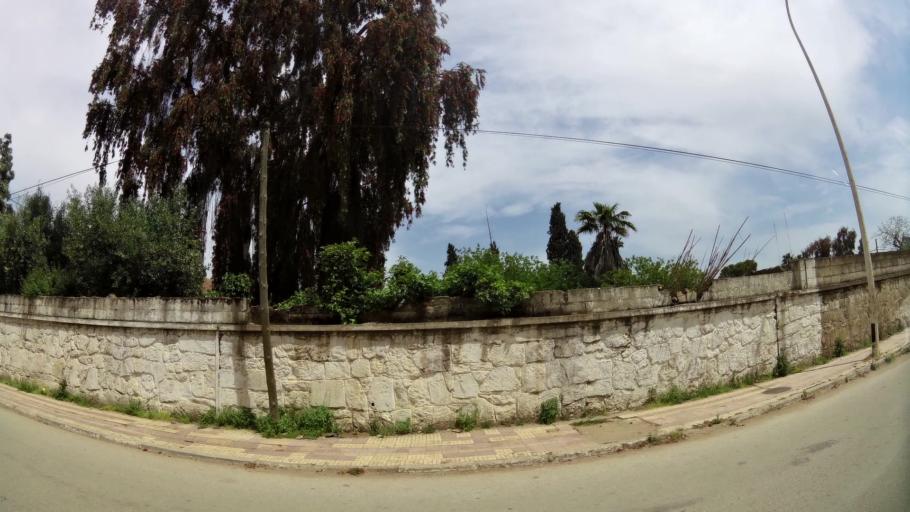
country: MA
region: Rabat-Sale-Zemmour-Zaer
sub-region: Khemisset
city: Khemisset
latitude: 33.8215
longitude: -6.0683
